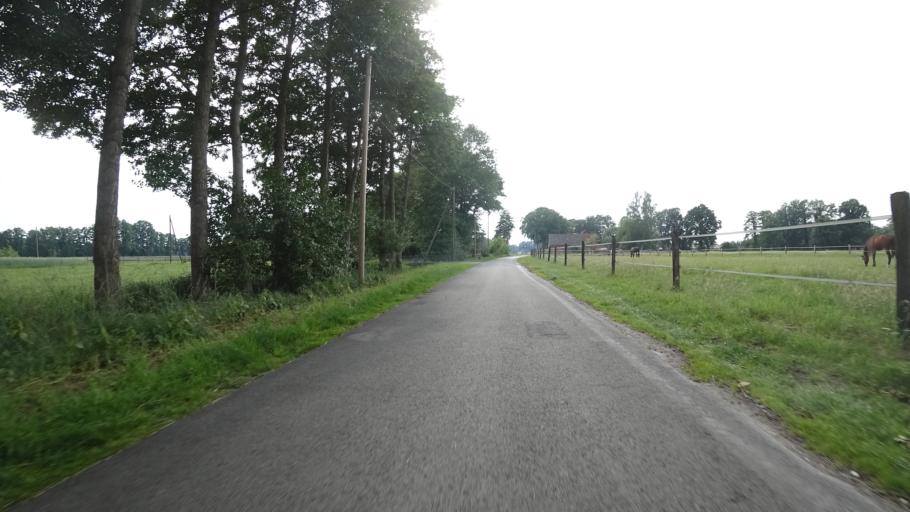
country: DE
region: North Rhine-Westphalia
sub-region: Regierungsbezirk Detmold
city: Guetersloh
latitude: 51.9471
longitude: 8.3668
